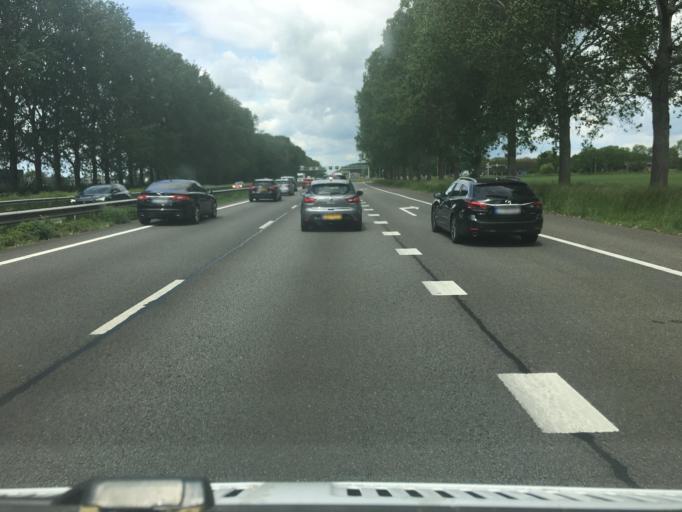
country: NL
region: Gelderland
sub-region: Gemeente Zevenaar
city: Zevenaar
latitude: 51.9363
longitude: 6.0955
